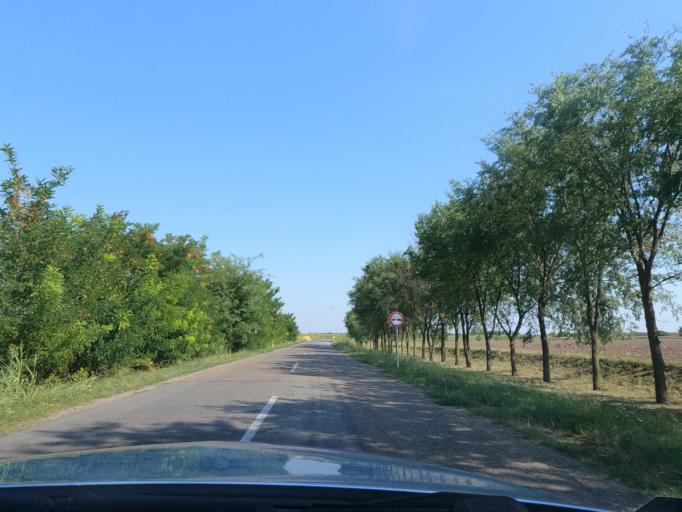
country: RS
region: Autonomna Pokrajina Vojvodina
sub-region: Juznobacki Okrug
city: Becej
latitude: 45.6592
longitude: 19.9567
